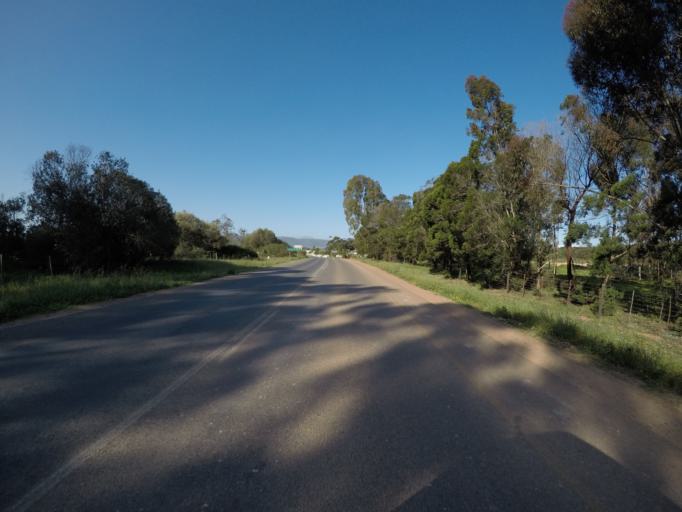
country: ZA
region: Western Cape
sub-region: City of Cape Town
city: Kraaifontein
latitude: -33.7667
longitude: 18.7863
